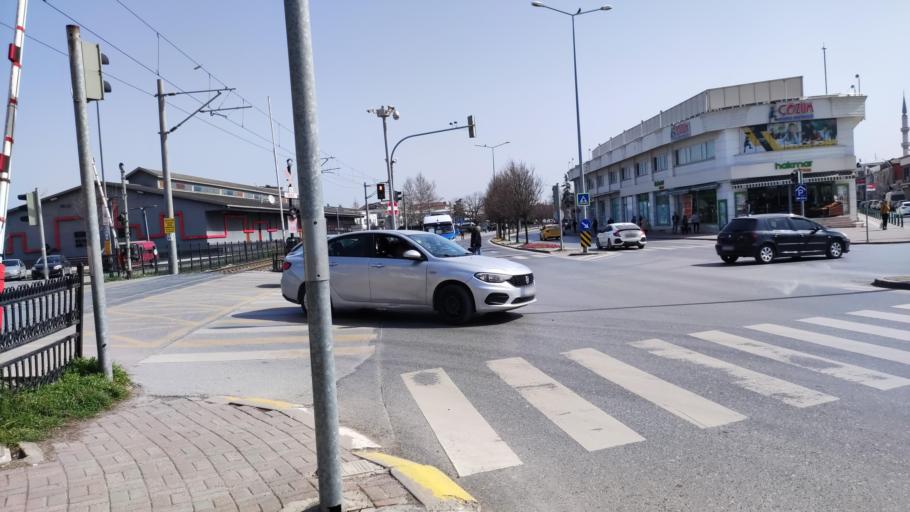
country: TR
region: Sakarya
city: Adapazari
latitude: 40.7719
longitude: 30.3922
